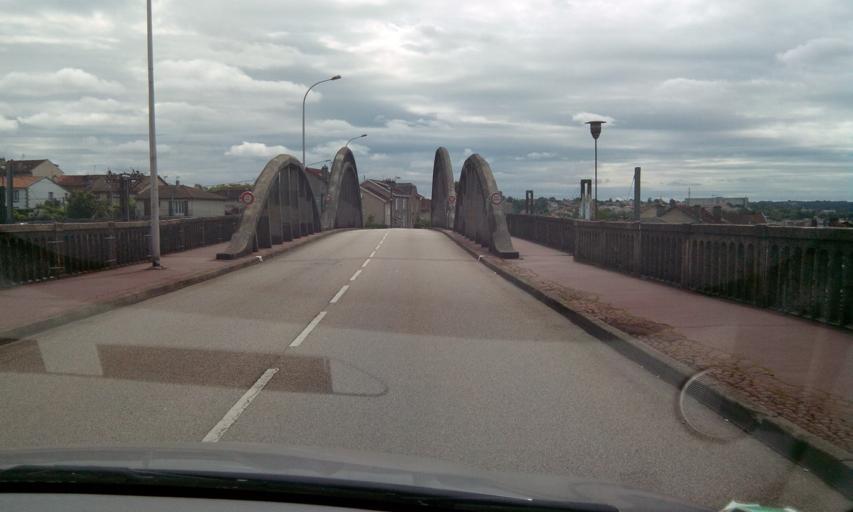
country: FR
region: Limousin
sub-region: Departement de la Haute-Vienne
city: Limoges
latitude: 45.8412
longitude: 1.2721
